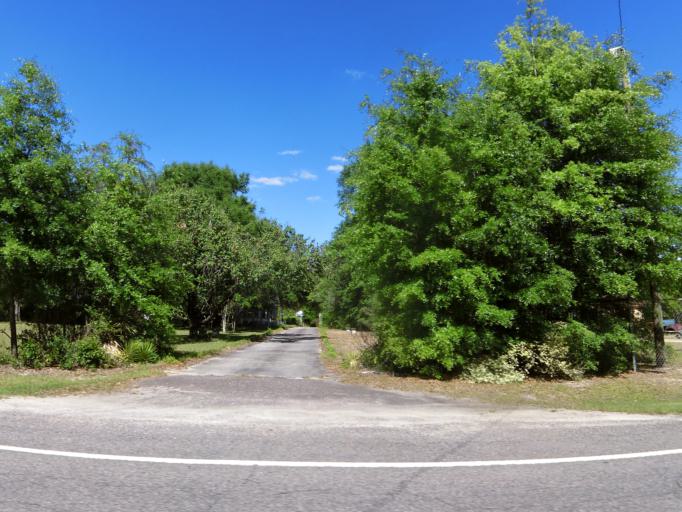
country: US
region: South Carolina
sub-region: Barnwell County
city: Williston
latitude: 33.4209
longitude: -81.4776
